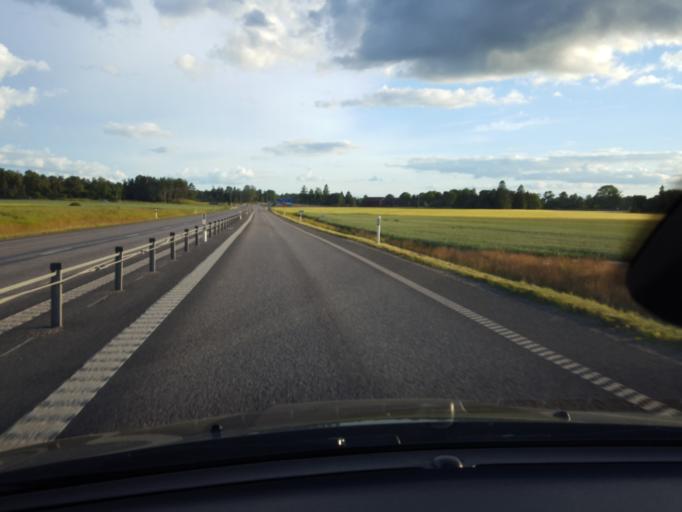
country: SE
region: Uppsala
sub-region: Uppsala Kommun
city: Vattholma
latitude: 59.9412
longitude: 17.8288
